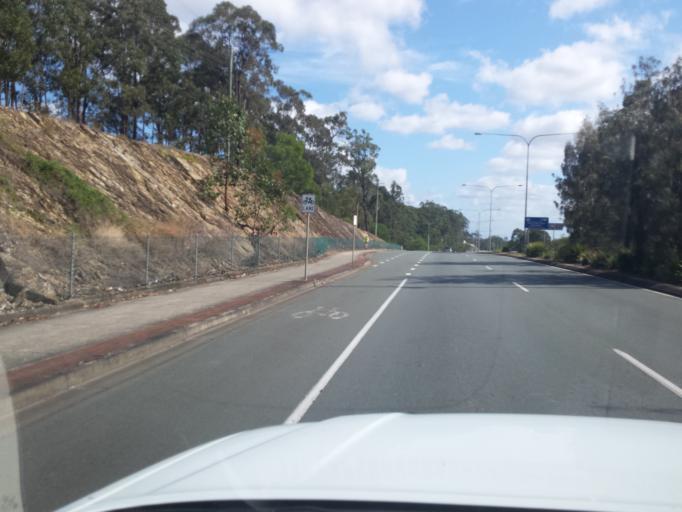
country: AU
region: Queensland
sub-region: Brisbane
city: Bridegman Downs
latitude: -27.3774
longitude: 152.9804
